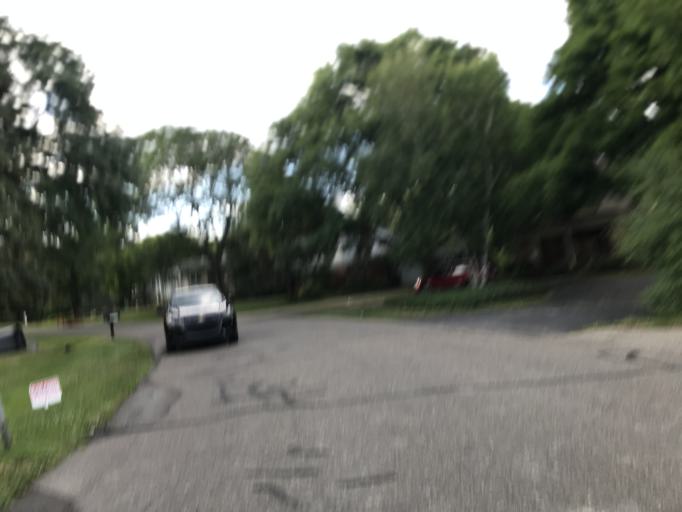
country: US
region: Michigan
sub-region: Oakland County
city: Farmington Hills
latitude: 42.4854
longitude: -83.3421
